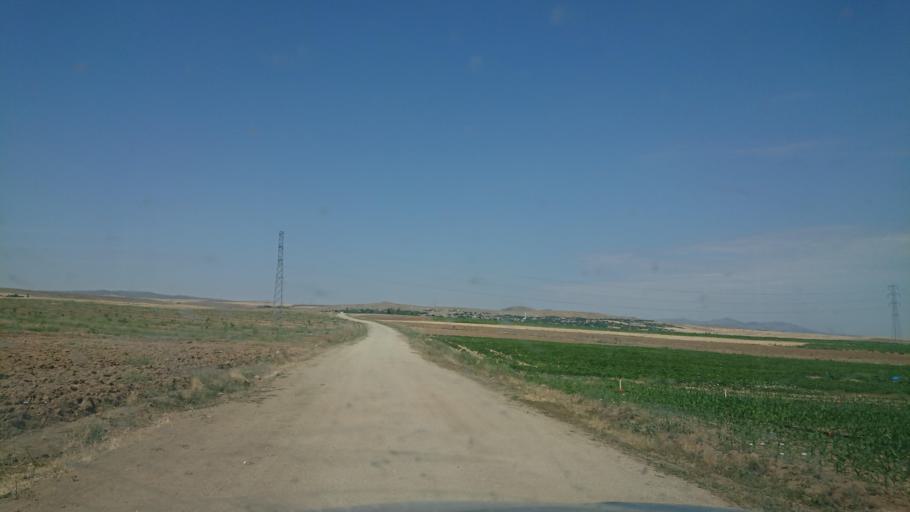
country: TR
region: Aksaray
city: Sariyahsi
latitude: 38.9577
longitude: 33.9097
